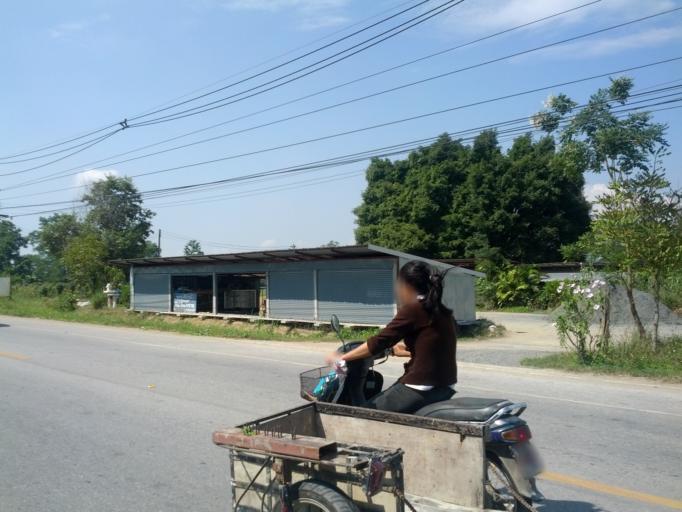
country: TH
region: Chiang Mai
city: San Kamphaeng
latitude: 18.7989
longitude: 99.1090
